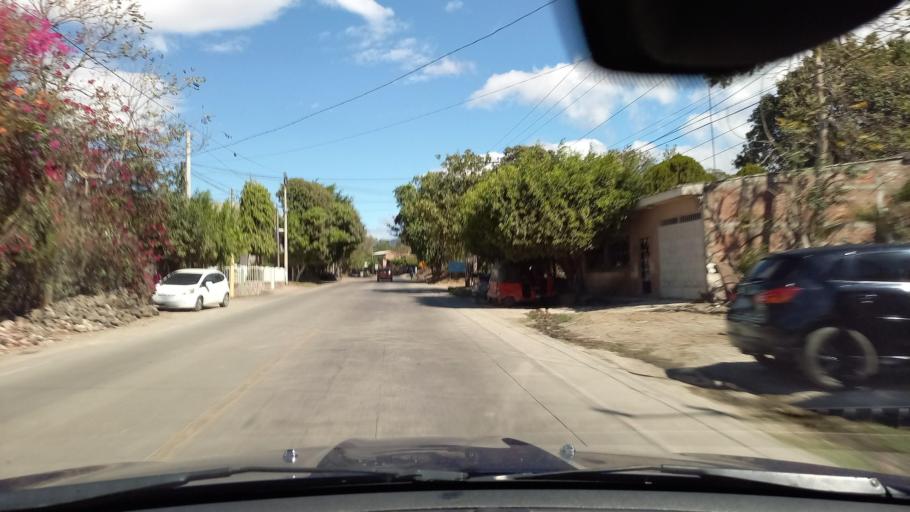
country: SV
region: Santa Ana
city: Metapan
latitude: 14.3491
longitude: -89.4531
